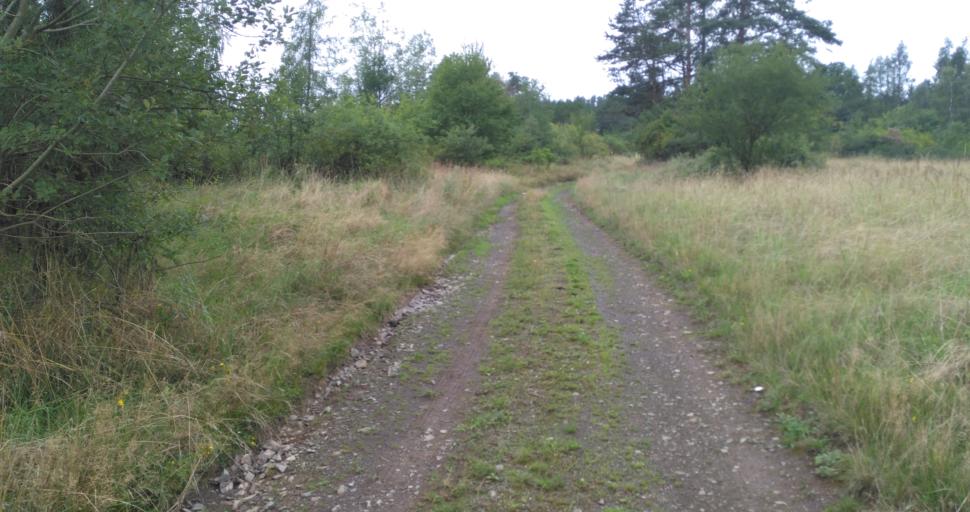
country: CZ
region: Central Bohemia
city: Jince
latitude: 49.7809
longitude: 13.9683
